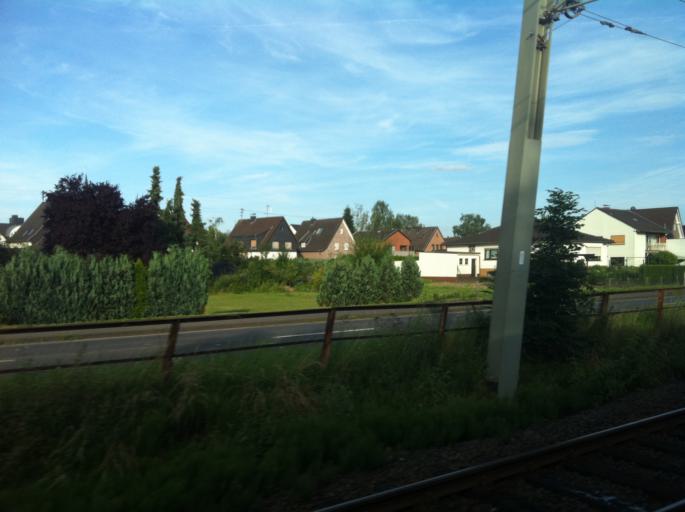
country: DE
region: North Rhine-Westphalia
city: Niederkassel
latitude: 50.7735
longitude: 7.0396
